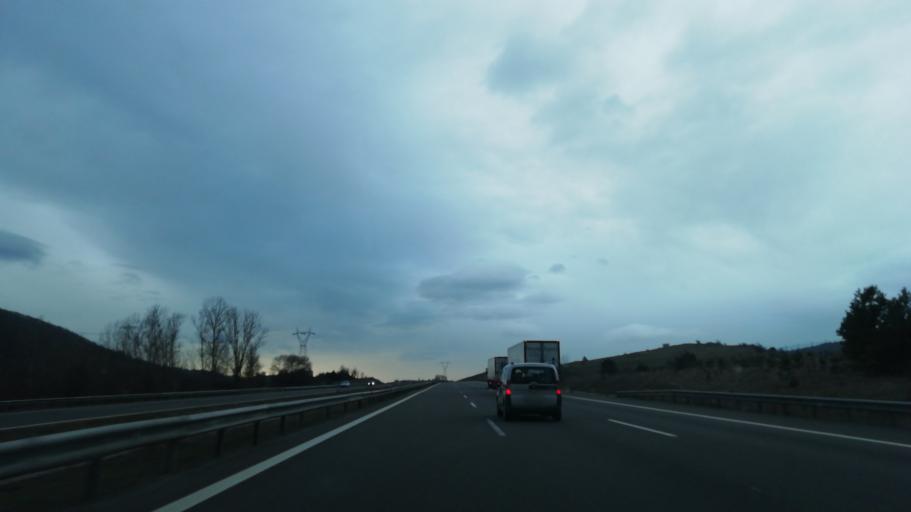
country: TR
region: Bolu
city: Yenicaga
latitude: 40.7620
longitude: 31.9870
